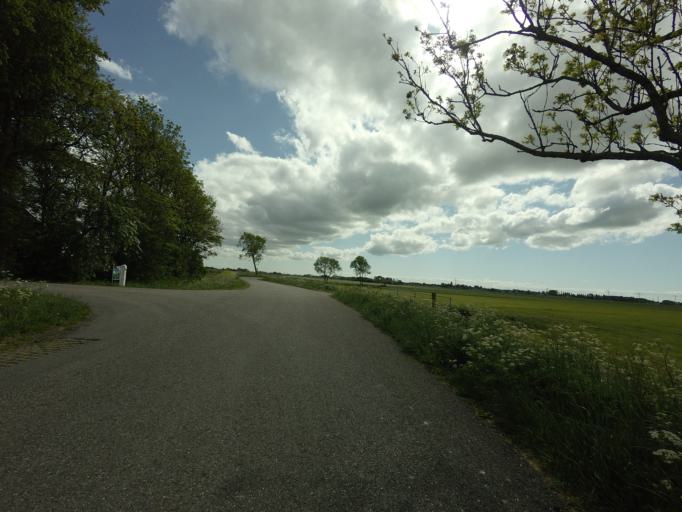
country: NL
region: Friesland
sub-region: Sudwest Fryslan
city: Bolsward
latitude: 53.0792
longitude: 5.5511
